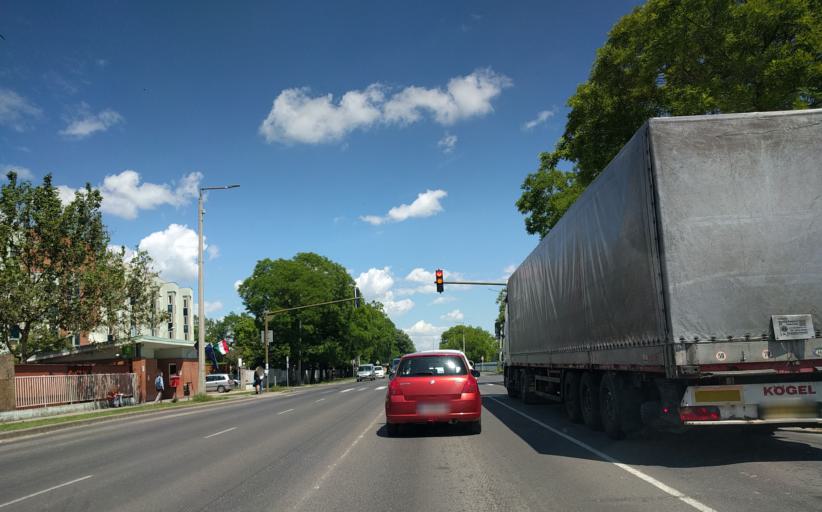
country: HU
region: Jasz-Nagykun-Szolnok
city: Szolnok
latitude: 47.1565
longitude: 20.1718
